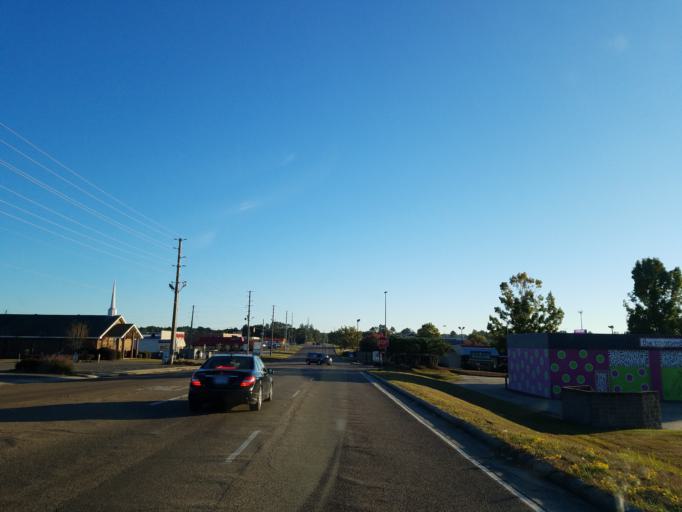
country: US
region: Mississippi
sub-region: Lamar County
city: West Hattiesburg
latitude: 31.3259
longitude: -89.3736
